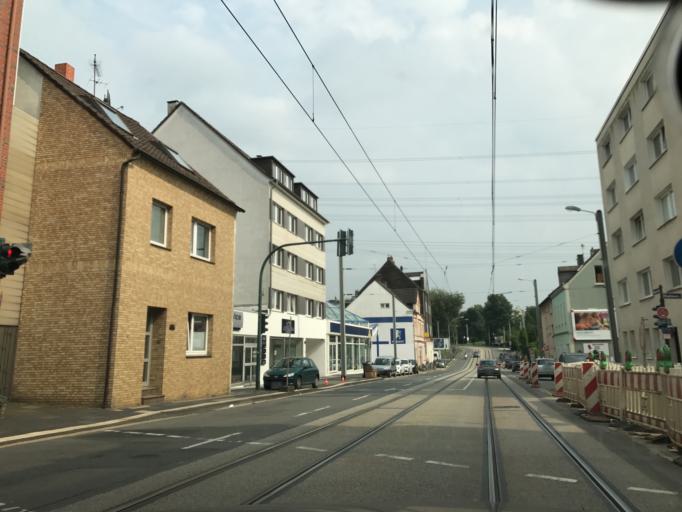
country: DE
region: North Rhine-Westphalia
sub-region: Regierungsbezirk Dusseldorf
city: Essen
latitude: 51.4628
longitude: 6.9579
